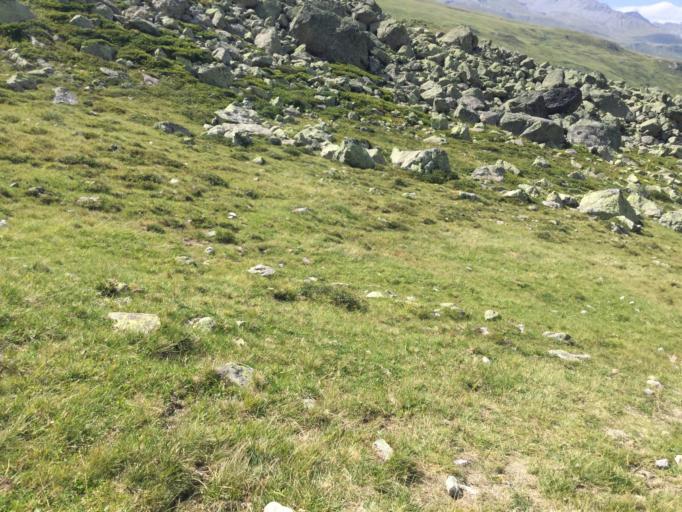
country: CH
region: Grisons
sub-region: Maloja District
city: Silvaplana
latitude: 46.4382
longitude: 9.6622
